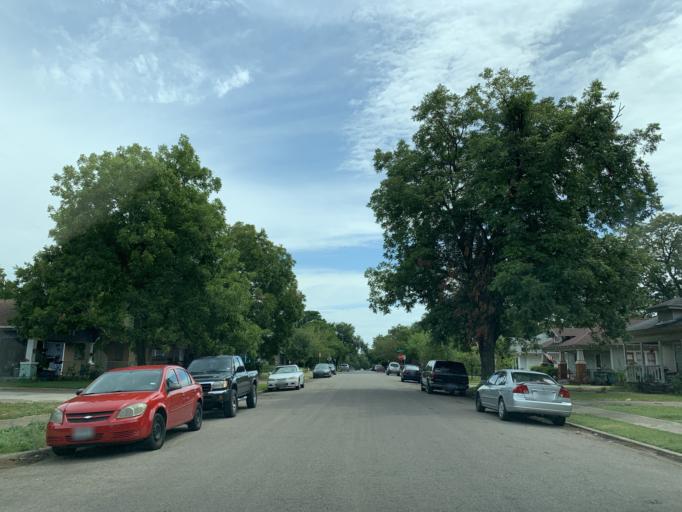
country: US
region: Texas
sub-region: Dallas County
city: Cockrell Hill
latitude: 32.7422
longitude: -96.8515
